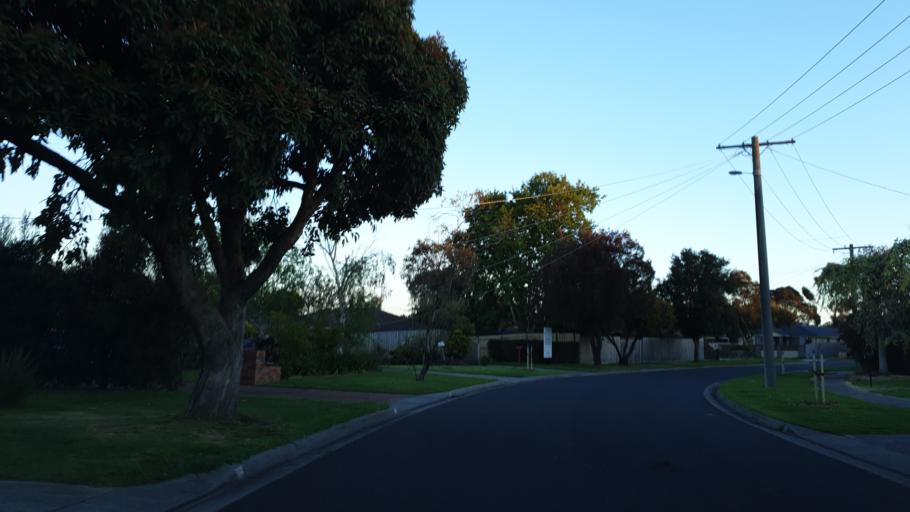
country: AU
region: Victoria
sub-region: Casey
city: Cranbourne
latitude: -38.0980
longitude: 145.2892
